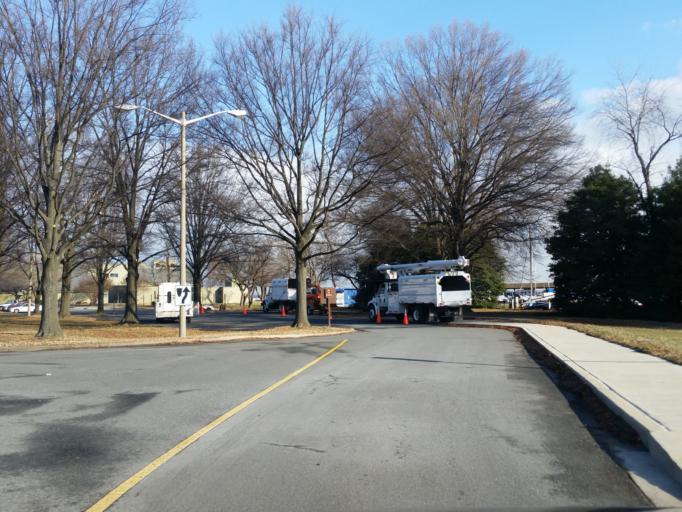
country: US
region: Virginia
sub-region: City of Alexandria
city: Alexandria
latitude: 38.8317
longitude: -77.0416
